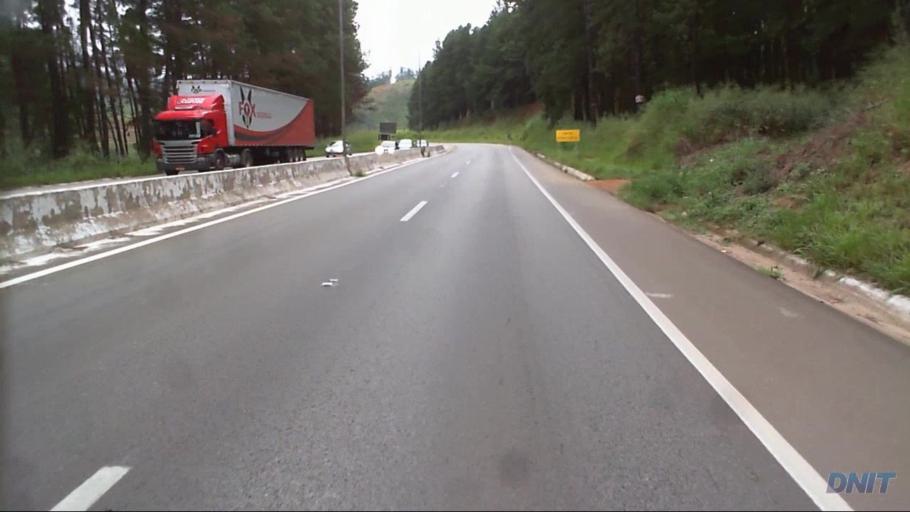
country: BR
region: Minas Gerais
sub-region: Nova Era
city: Nova Era
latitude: -19.7702
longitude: -43.0471
